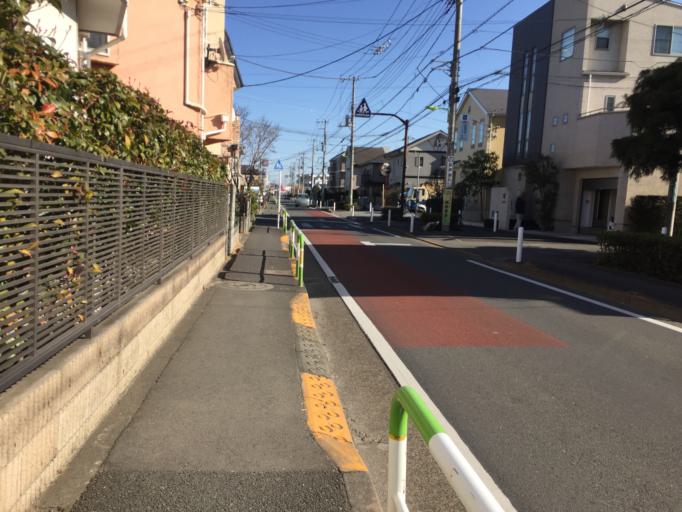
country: JP
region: Tokyo
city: Chofugaoka
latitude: 35.6229
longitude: 139.6056
